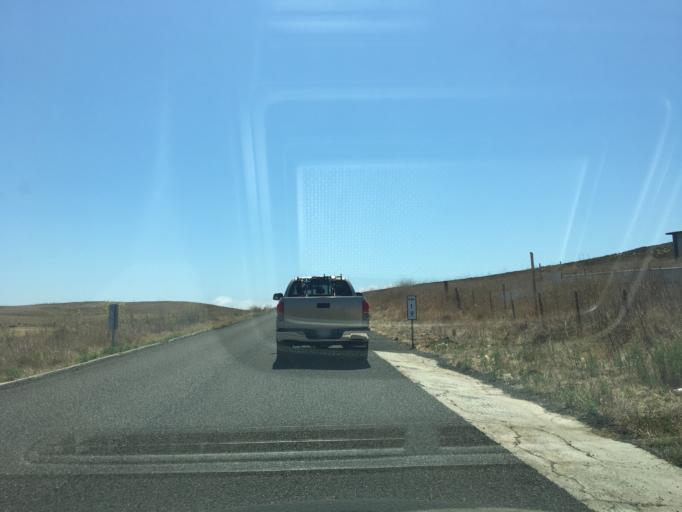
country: MX
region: Baja California
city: El Sauzal
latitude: 31.9907
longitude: -116.7087
